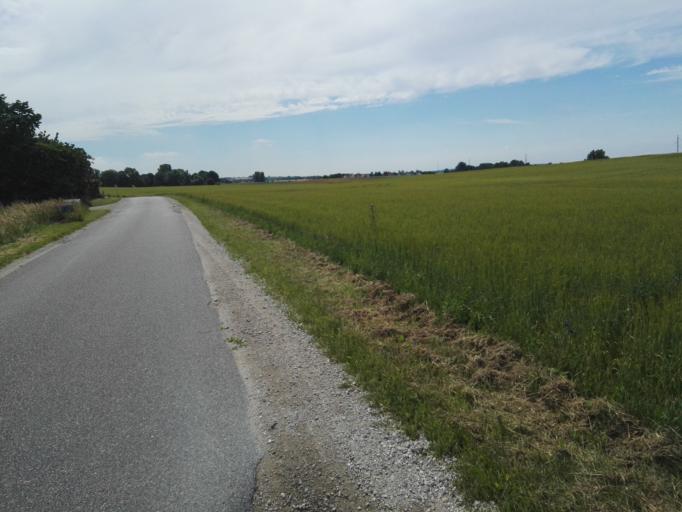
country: DK
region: Capital Region
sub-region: Hillerod Kommune
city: Skaevinge
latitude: 55.8885
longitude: 12.1311
